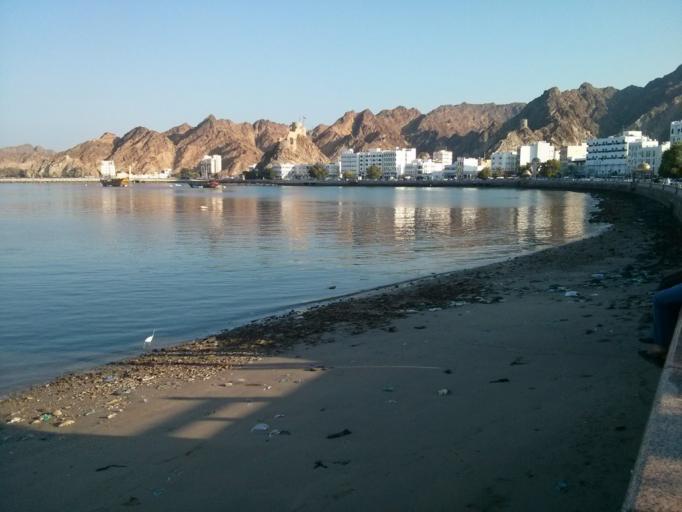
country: OM
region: Muhafazat Masqat
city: Muscat
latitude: 23.6229
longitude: 58.5622
